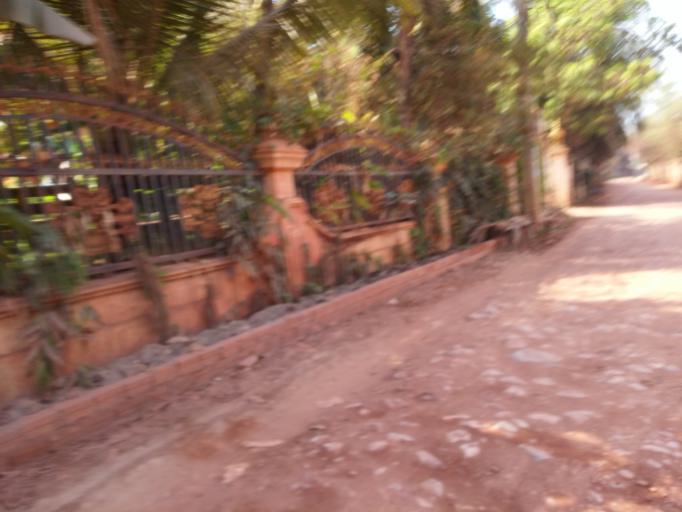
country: KH
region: Siem Reap
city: Siem Reap
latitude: 13.3704
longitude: 103.8475
